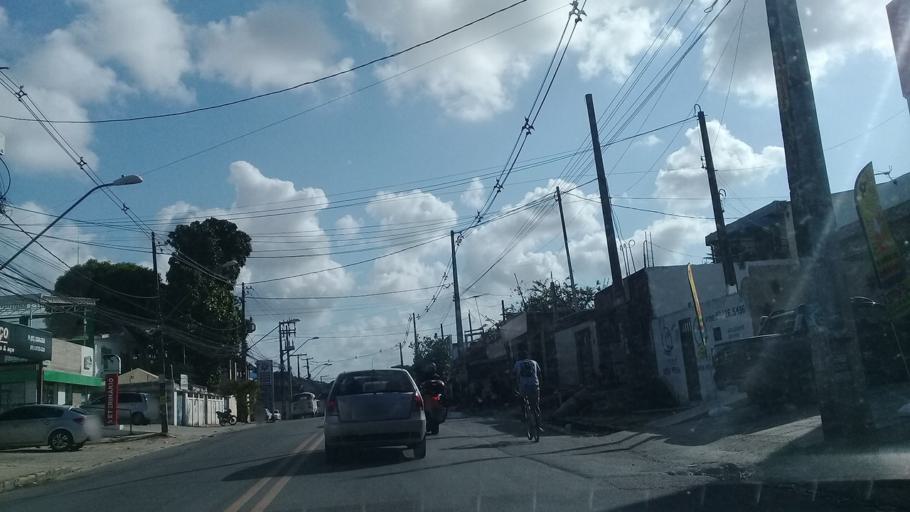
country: BR
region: Pernambuco
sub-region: Jaboatao Dos Guararapes
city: Jaboatao dos Guararapes
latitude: -8.1122
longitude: -34.9380
